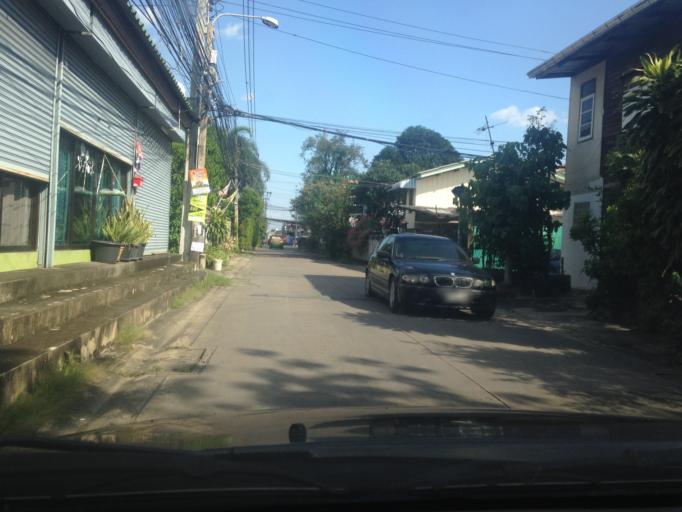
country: TH
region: Nonthaburi
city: Pak Kret
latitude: 13.8872
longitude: 100.5022
